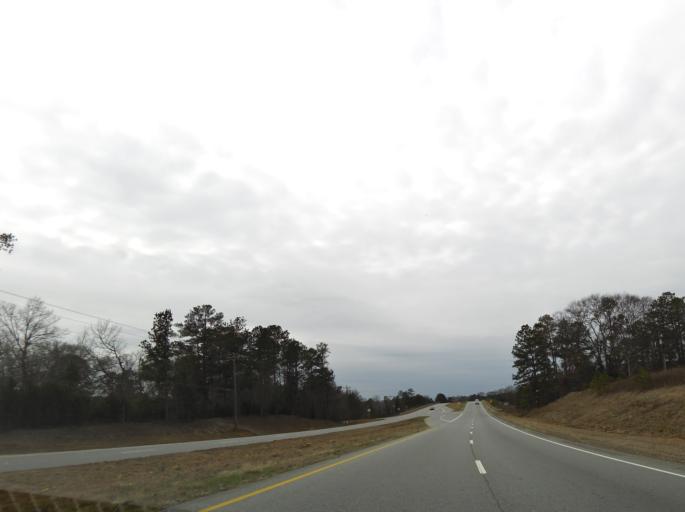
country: US
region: Georgia
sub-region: Peach County
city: Byron
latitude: 32.6367
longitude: -83.7699
